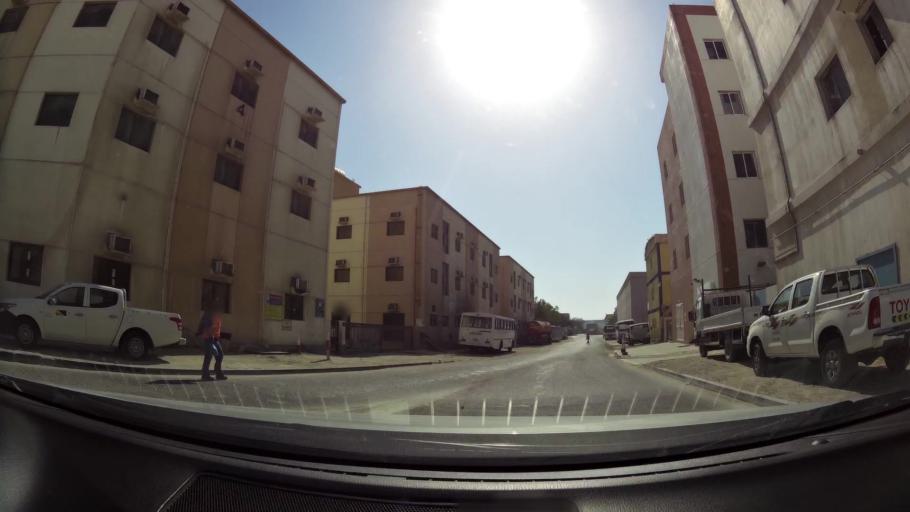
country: AE
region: Dubai
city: Dubai
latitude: 25.0043
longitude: 55.1032
